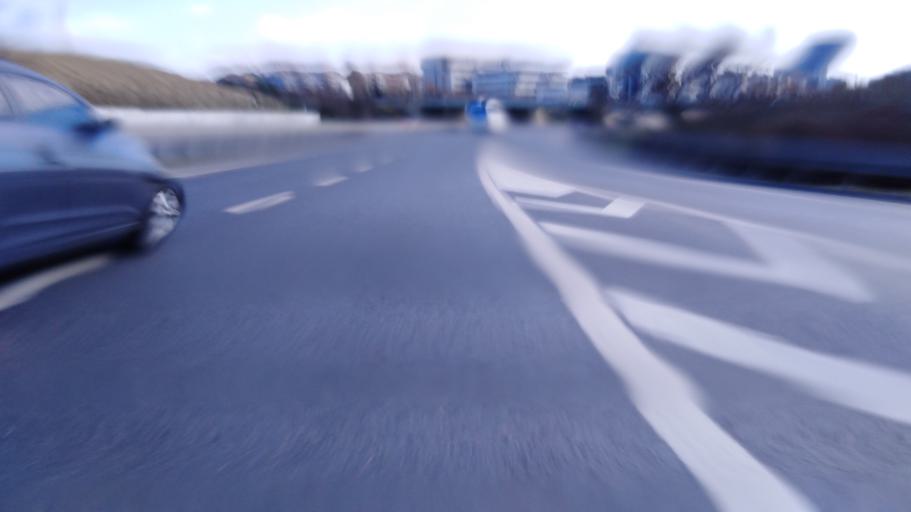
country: TR
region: Istanbul
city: Esenler
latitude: 41.0584
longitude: 28.8879
